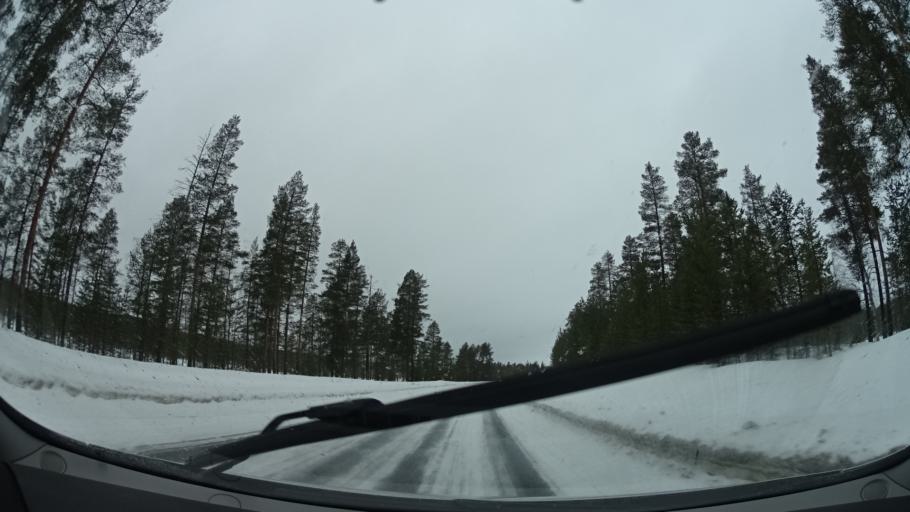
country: SE
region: Vaesterbotten
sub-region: Mala Kommun
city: Mala
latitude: 65.1456
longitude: 18.8248
